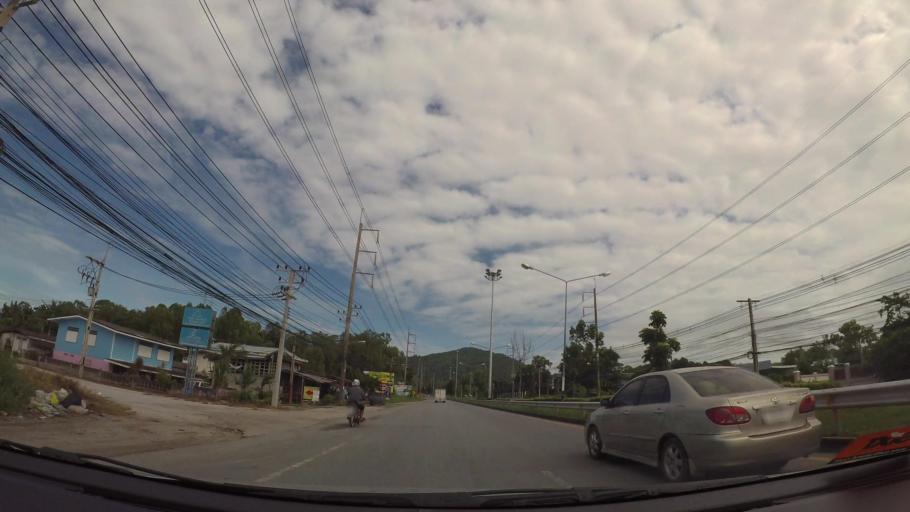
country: TH
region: Rayong
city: Ban Chang
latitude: 12.7468
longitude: 101.1110
